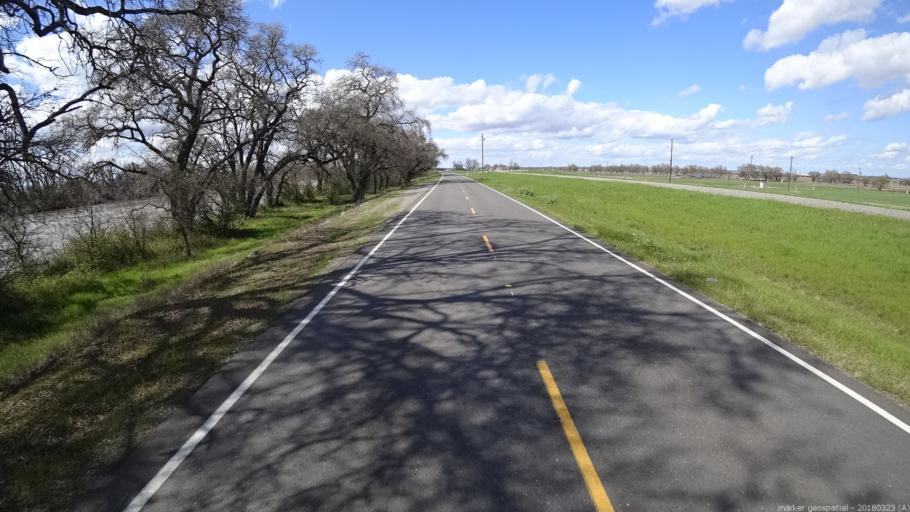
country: US
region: California
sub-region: Yolo County
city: West Sacramento
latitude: 38.6588
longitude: -121.6050
